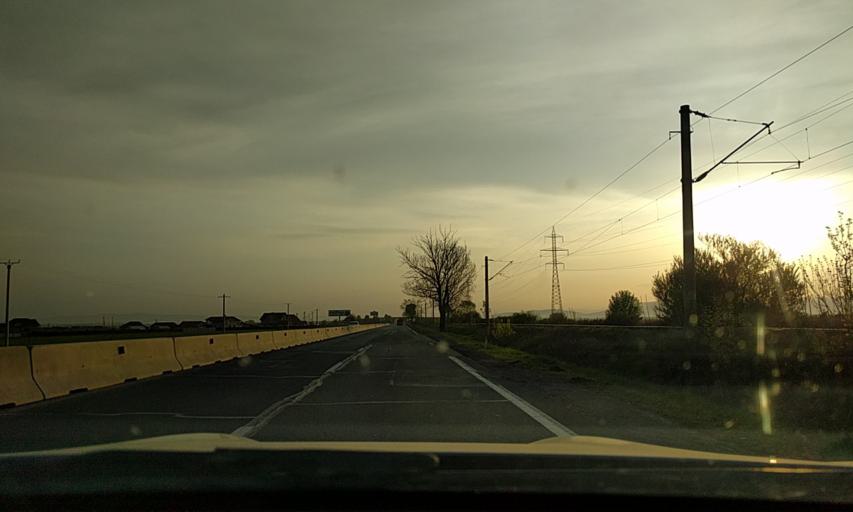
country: RO
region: Brasov
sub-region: Comuna Harman
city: Harman
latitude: 45.7056
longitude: 25.6981
